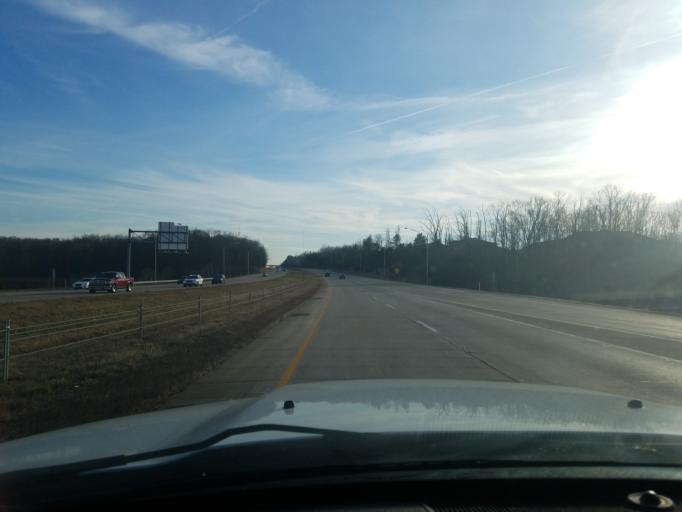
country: US
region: Indiana
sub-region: Bartholomew County
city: Columbus
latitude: 39.1976
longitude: -85.9588
